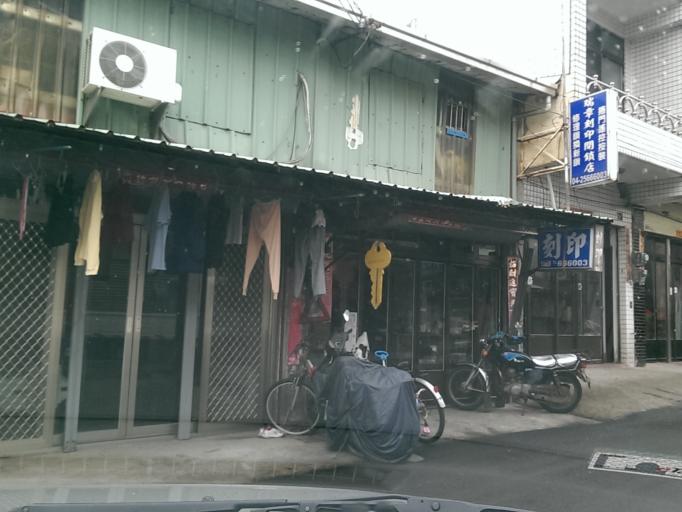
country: TW
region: Taiwan
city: Fengyuan
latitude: 24.2341
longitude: 120.6239
